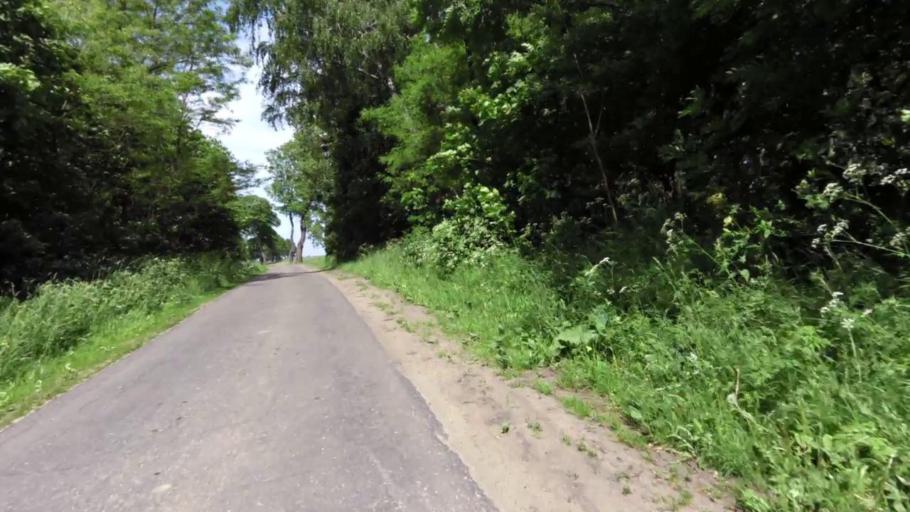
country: PL
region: West Pomeranian Voivodeship
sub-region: Powiat szczecinecki
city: Szczecinek
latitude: 53.6436
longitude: 16.6824
